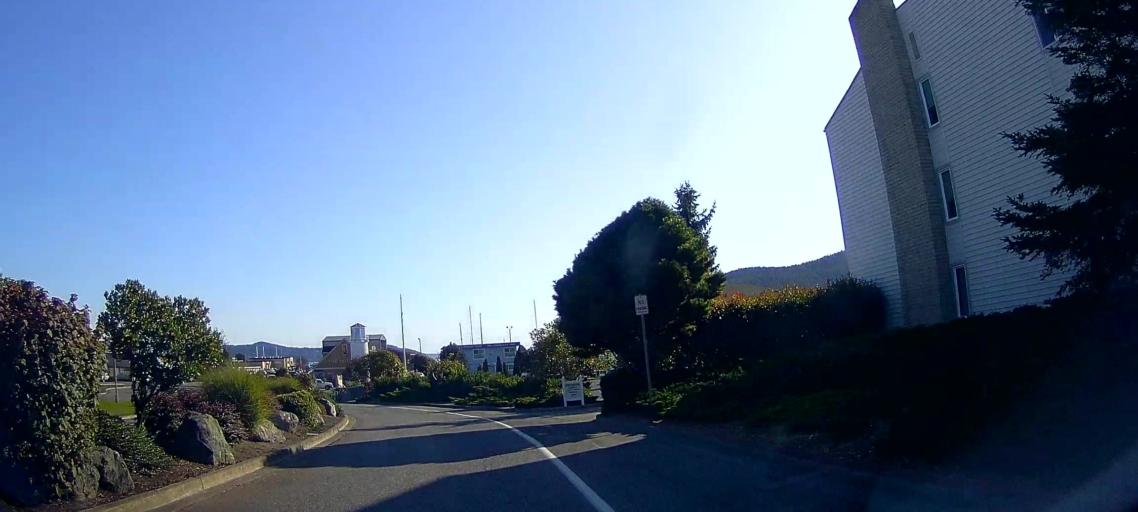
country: US
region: Washington
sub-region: Skagit County
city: Anacortes
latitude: 48.4960
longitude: -122.6854
